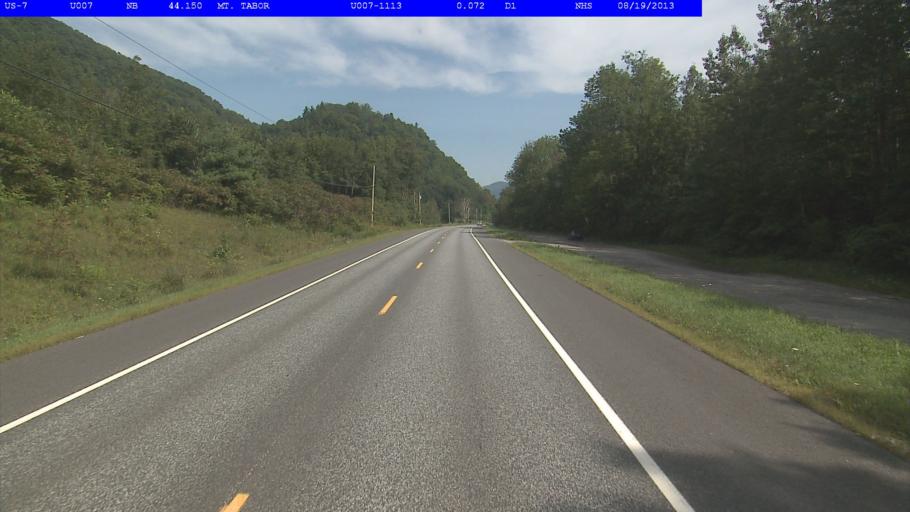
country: US
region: Vermont
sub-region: Bennington County
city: Manchester Center
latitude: 43.3061
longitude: -72.9948
